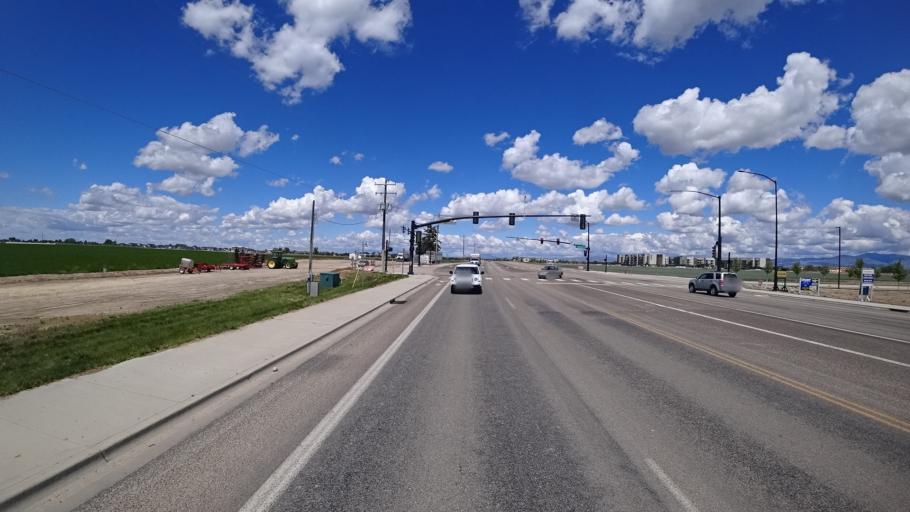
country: US
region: Idaho
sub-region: Ada County
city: Meridian
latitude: 43.5981
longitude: -116.4342
